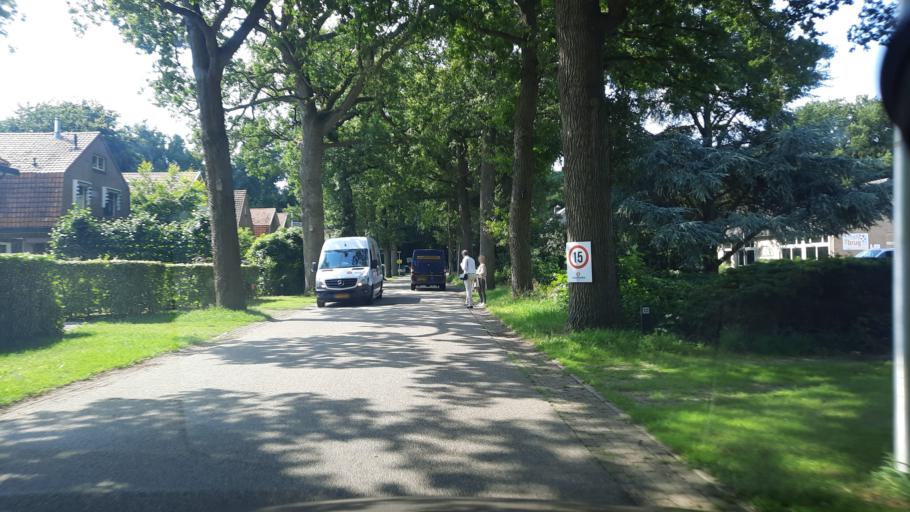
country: NL
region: Gelderland
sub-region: Gemeente Hattem
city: Hattem
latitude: 52.4994
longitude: 6.0683
